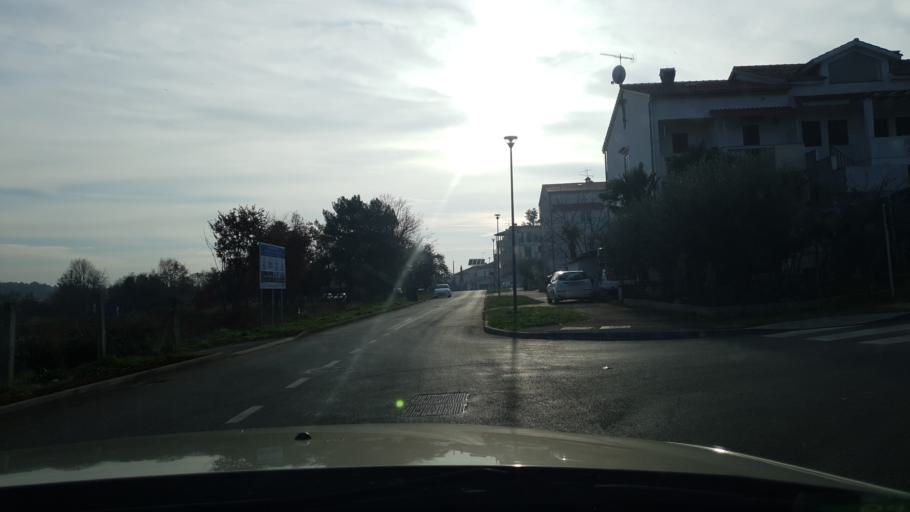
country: HR
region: Istarska
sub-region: Grad Porec
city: Porec
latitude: 45.2343
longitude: 13.6105
